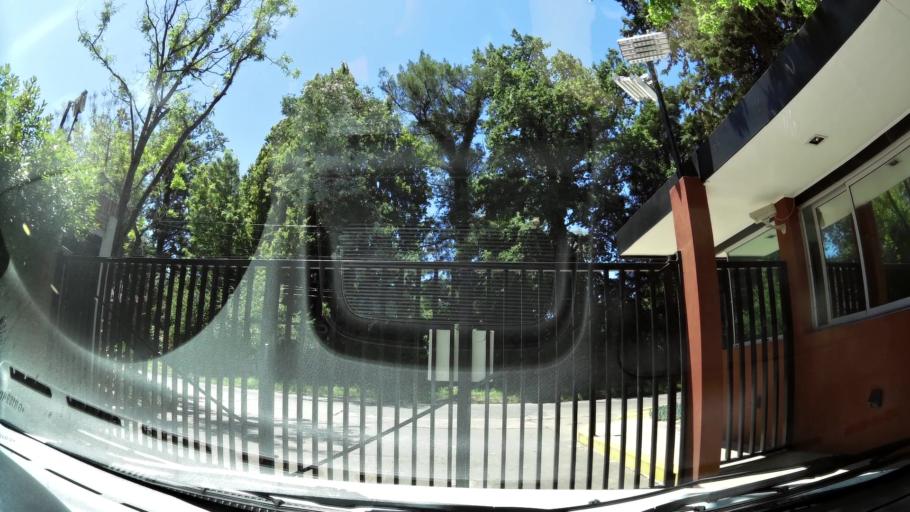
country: AR
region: Buenos Aires
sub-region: Partido de San Isidro
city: San Isidro
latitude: -34.4941
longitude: -58.5721
